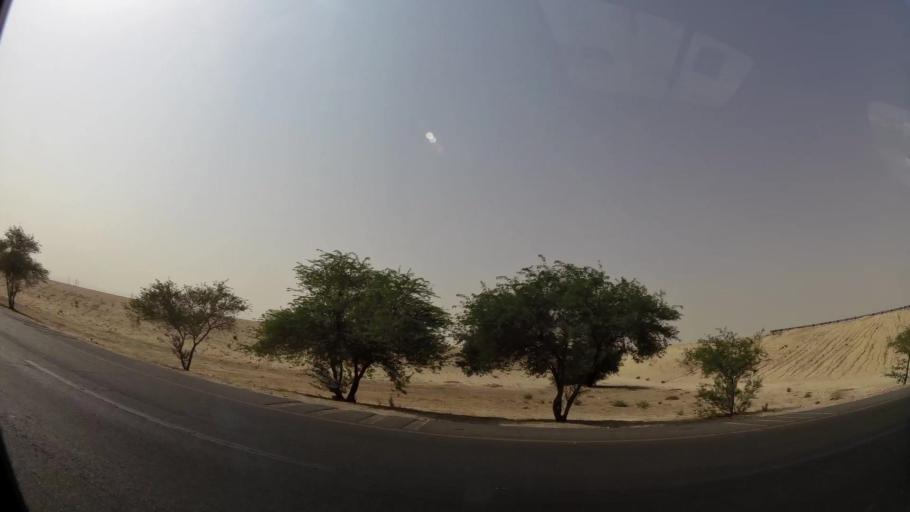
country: KW
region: Muhafazat al Jahra'
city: Al Jahra'
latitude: 29.3241
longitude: 47.6383
